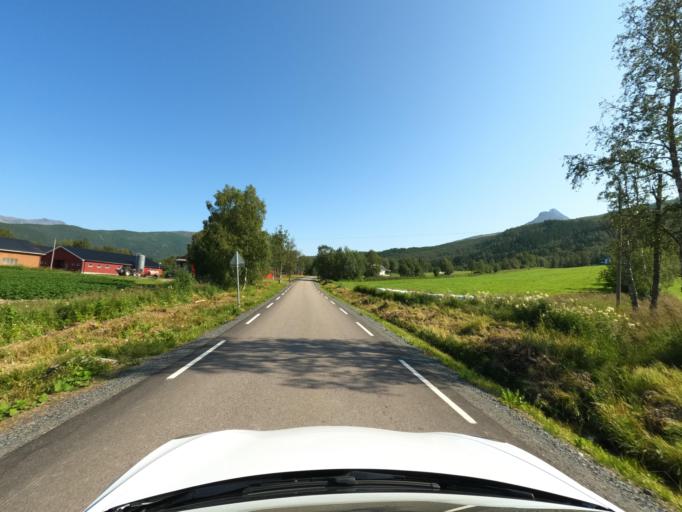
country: NO
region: Nordland
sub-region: Narvik
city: Narvik
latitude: 68.3975
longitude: 17.2978
